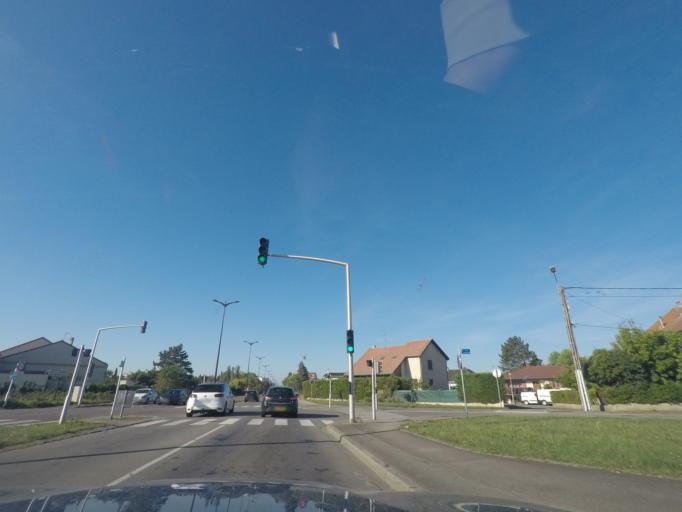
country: FR
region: Lorraine
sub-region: Departement de la Moselle
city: Thionville
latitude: 49.3714
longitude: 6.1639
